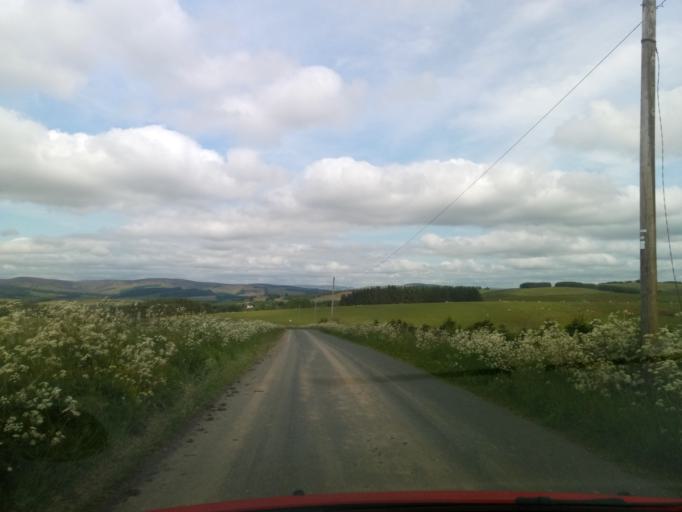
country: GB
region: Scotland
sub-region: The Scottish Borders
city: Selkirk
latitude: 55.5188
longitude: -2.8165
